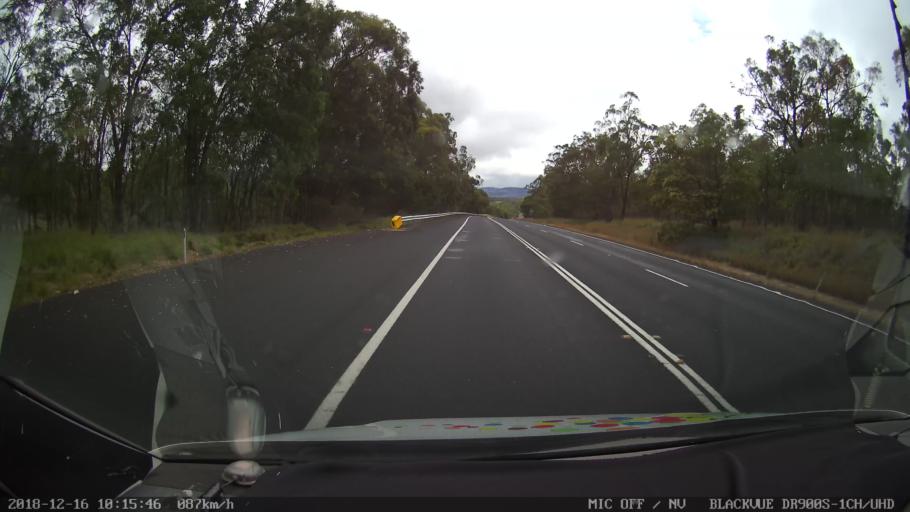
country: AU
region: New South Wales
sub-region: Tenterfield Municipality
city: Carrolls Creek
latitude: -29.2740
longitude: 151.9756
